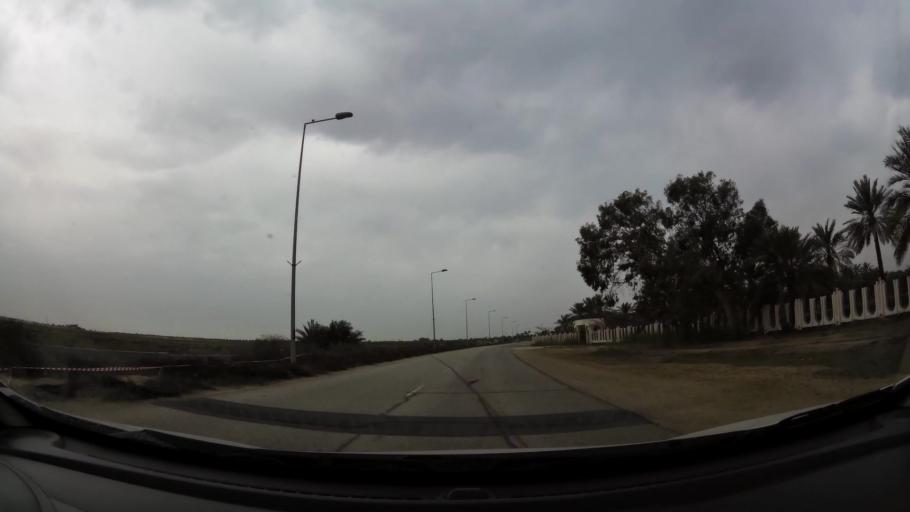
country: BH
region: Central Governorate
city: Dar Kulayb
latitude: 26.0281
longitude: 50.4818
